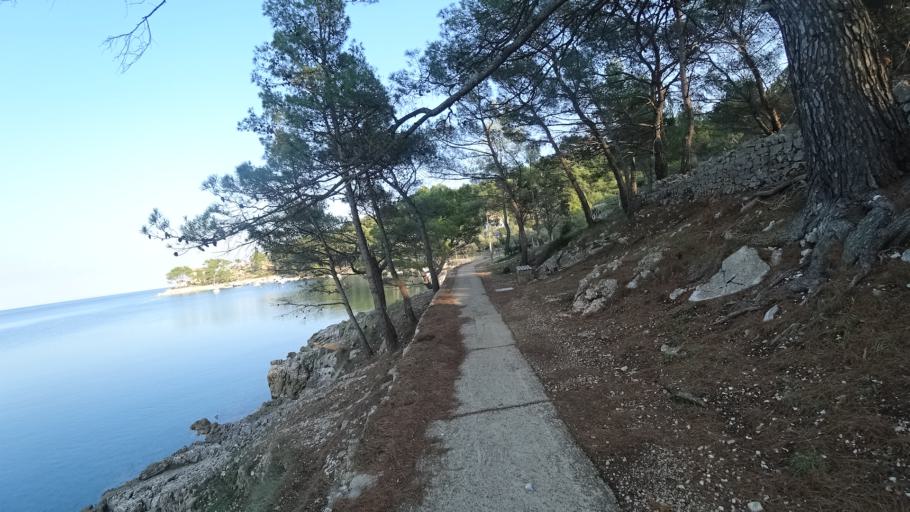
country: HR
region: Primorsko-Goranska
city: Mali Losinj
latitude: 44.5268
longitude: 14.4811
